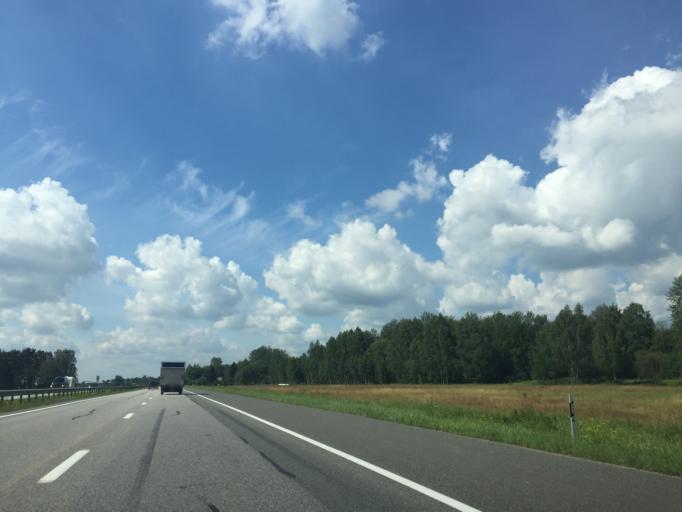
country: LV
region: Olaine
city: Olaine
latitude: 56.8124
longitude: 24.0040
